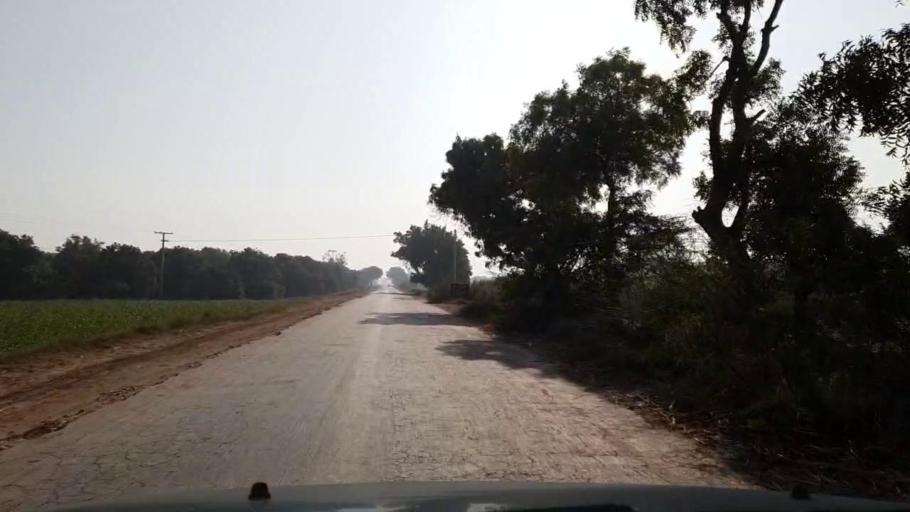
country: PK
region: Sindh
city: Matiari
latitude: 25.5564
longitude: 68.5342
